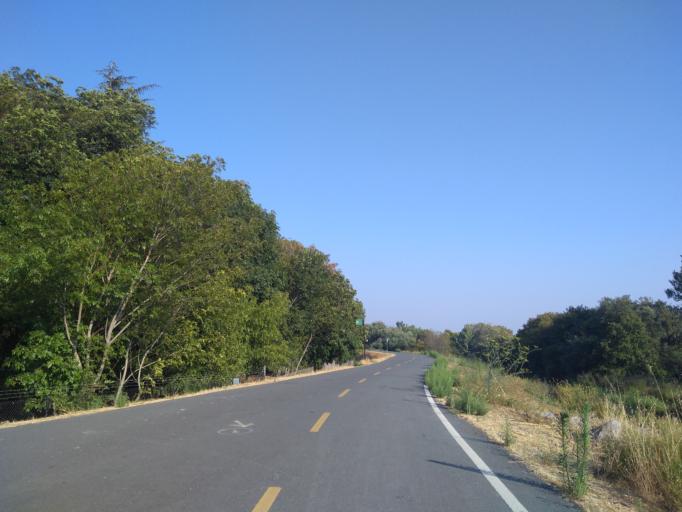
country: US
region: California
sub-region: Santa Clara County
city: Santa Clara
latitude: 37.3795
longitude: -121.9372
